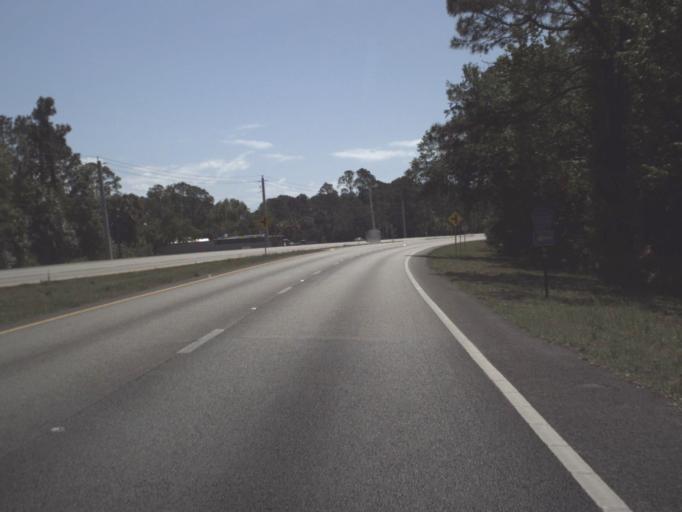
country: US
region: Florida
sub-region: Flagler County
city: Bunnell
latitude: 29.4082
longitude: -81.1991
